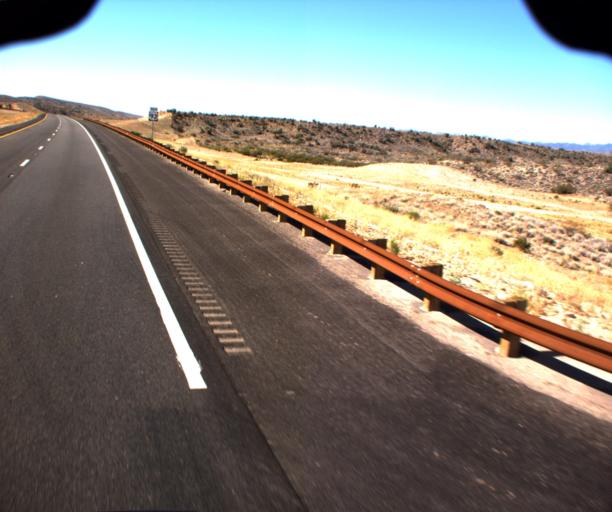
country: US
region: Arizona
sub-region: Mohave County
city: Kingman
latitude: 35.0045
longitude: -113.6647
